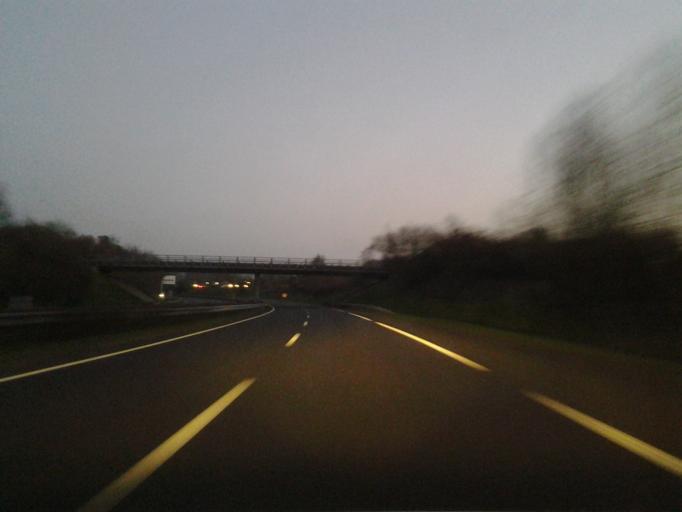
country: FR
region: Pays de la Loire
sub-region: Departement de la Vendee
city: Challans
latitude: 46.8411
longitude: -1.8524
